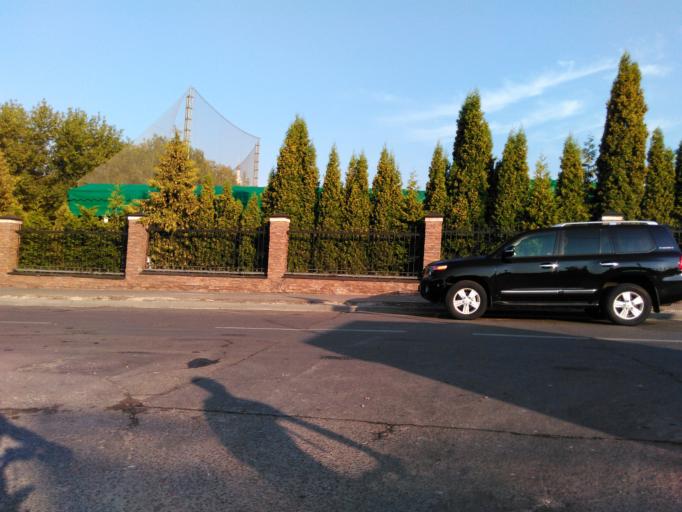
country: RU
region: Moscow
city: Vorob'yovo
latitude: 55.7230
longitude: 37.5171
